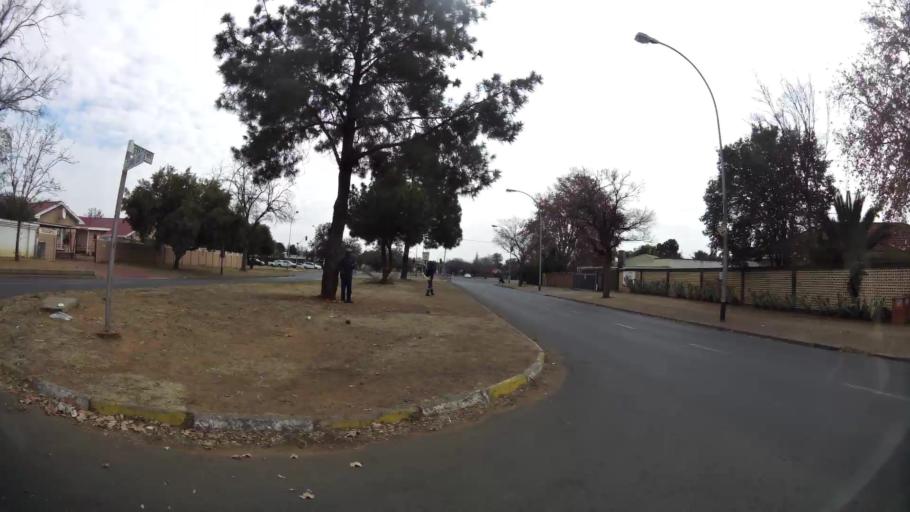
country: ZA
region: Orange Free State
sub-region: Mangaung Metropolitan Municipality
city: Bloemfontein
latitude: -29.1272
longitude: 26.1777
